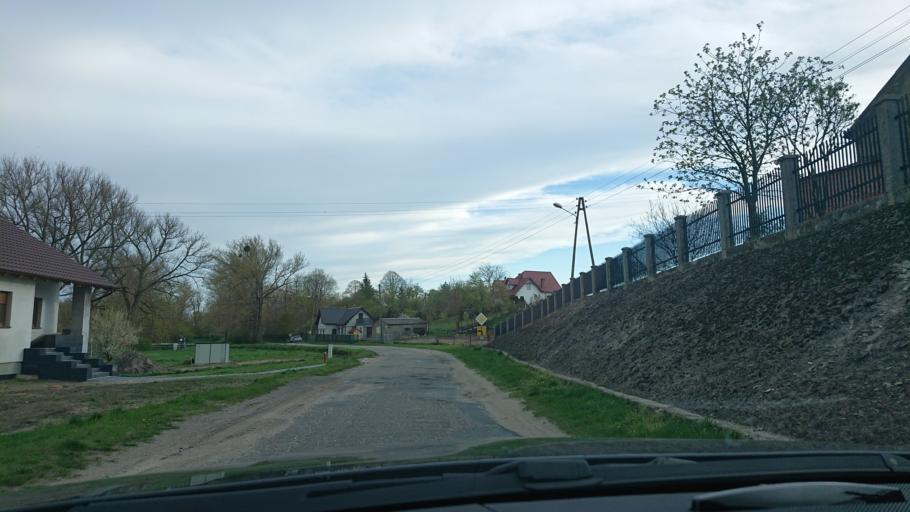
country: PL
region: Greater Poland Voivodeship
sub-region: Powiat gnieznienski
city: Lubowo
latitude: 52.5763
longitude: 17.4713
